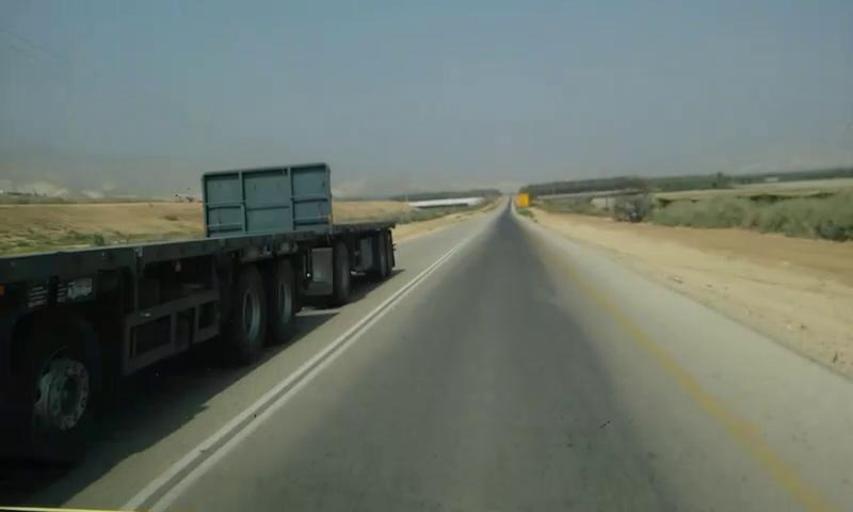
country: PS
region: West Bank
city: Al `Awja
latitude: 31.9873
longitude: 35.4615
